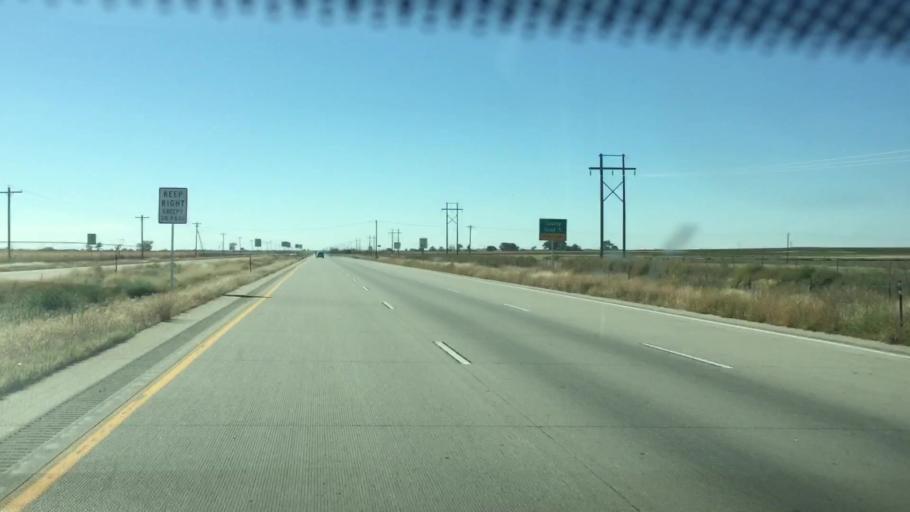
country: US
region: Colorado
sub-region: Prowers County
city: Lamar
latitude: 38.1110
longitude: -102.6656
